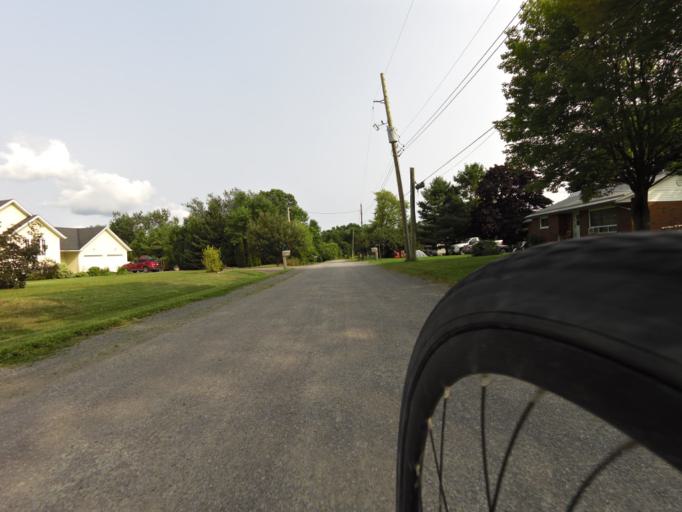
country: CA
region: Ontario
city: Quinte West
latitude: 44.0485
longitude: -77.6283
